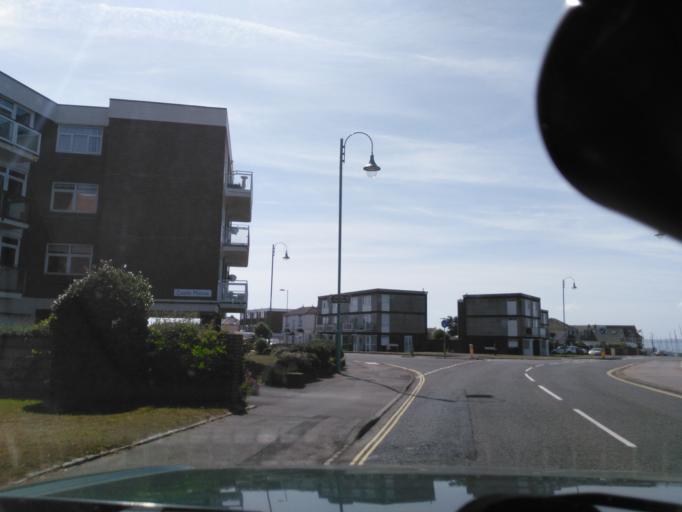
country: GB
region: England
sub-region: Hampshire
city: Lee-on-the-Solent
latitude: 50.7962
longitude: -1.1972
